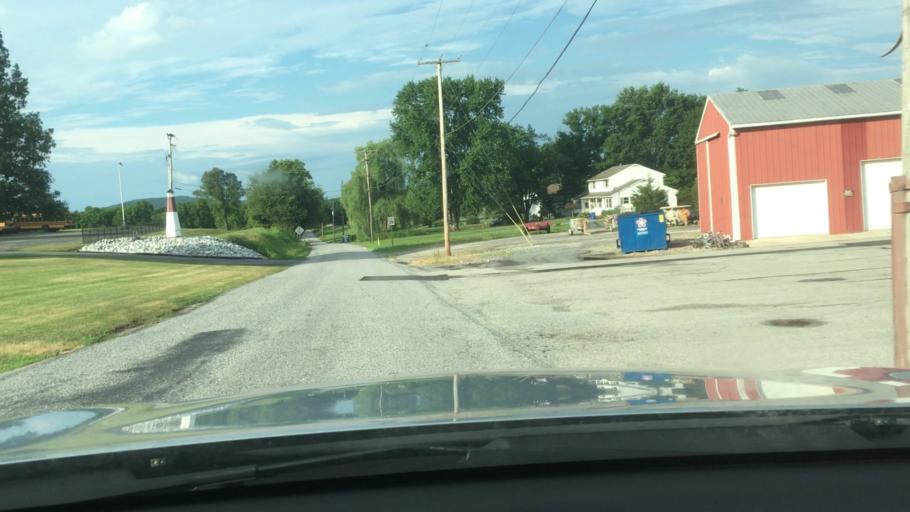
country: US
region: Pennsylvania
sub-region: York County
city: Dover
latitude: 40.0115
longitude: -76.8593
